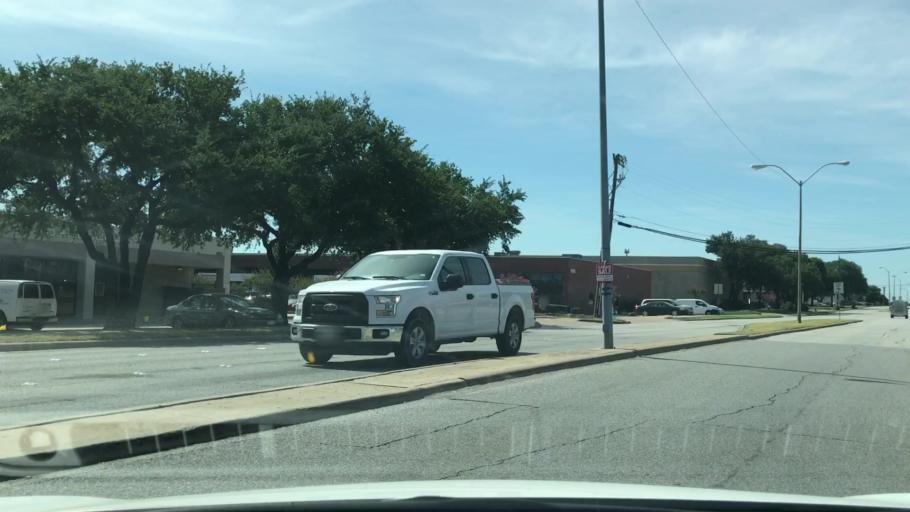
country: US
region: Texas
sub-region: Dallas County
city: Richardson
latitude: 32.9605
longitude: -96.7138
